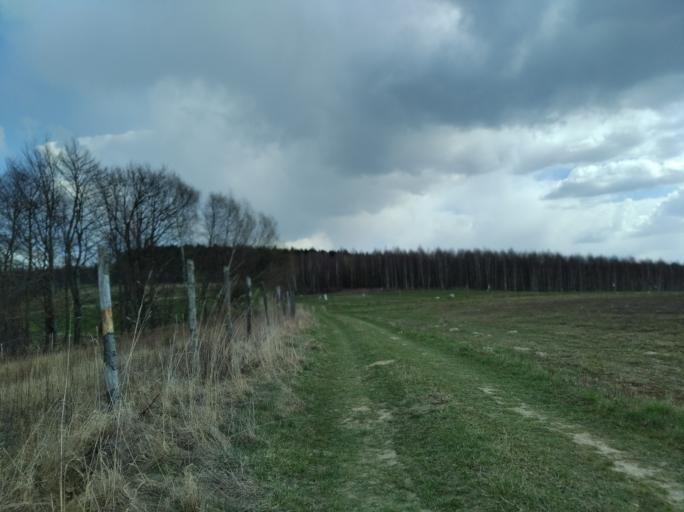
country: PL
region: Subcarpathian Voivodeship
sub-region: Powiat strzyzowski
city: Strzyzow
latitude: 49.9089
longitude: 21.7645
